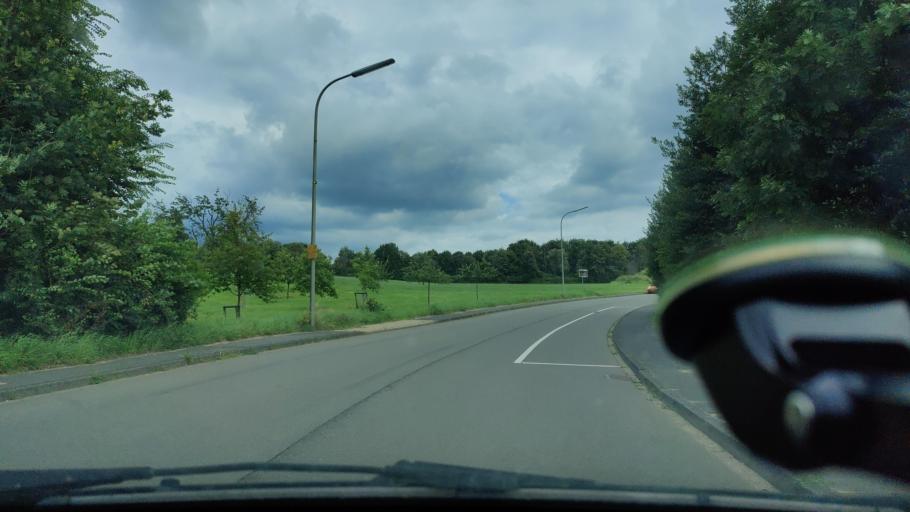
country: DE
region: North Rhine-Westphalia
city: Burscheid
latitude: 51.0817
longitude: 7.1254
